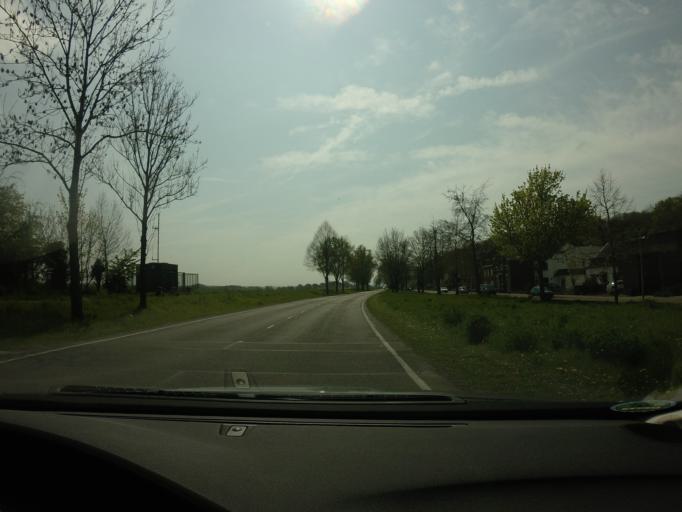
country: NL
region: Limburg
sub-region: Gemeente Maastricht
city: Maastricht
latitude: 50.8307
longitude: 5.6957
